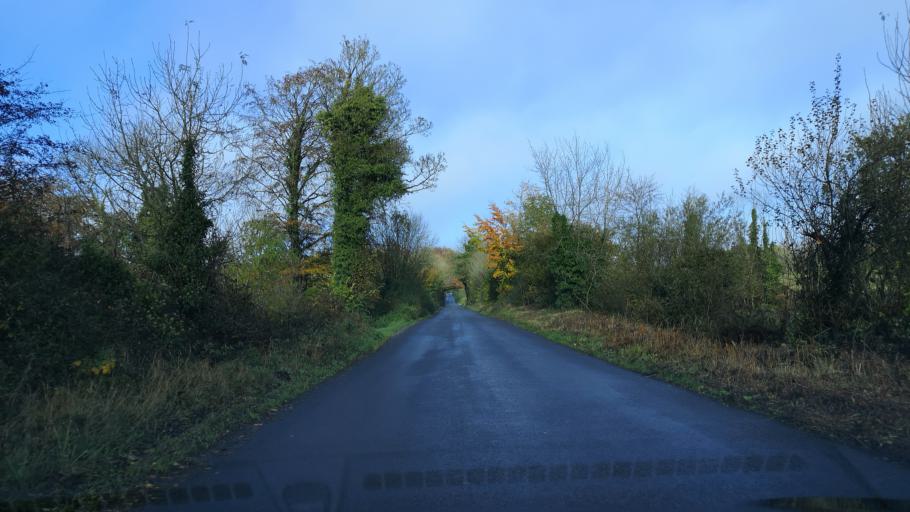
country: IE
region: Leinster
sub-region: An Iarmhi
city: Moate
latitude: 53.3850
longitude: -7.8048
